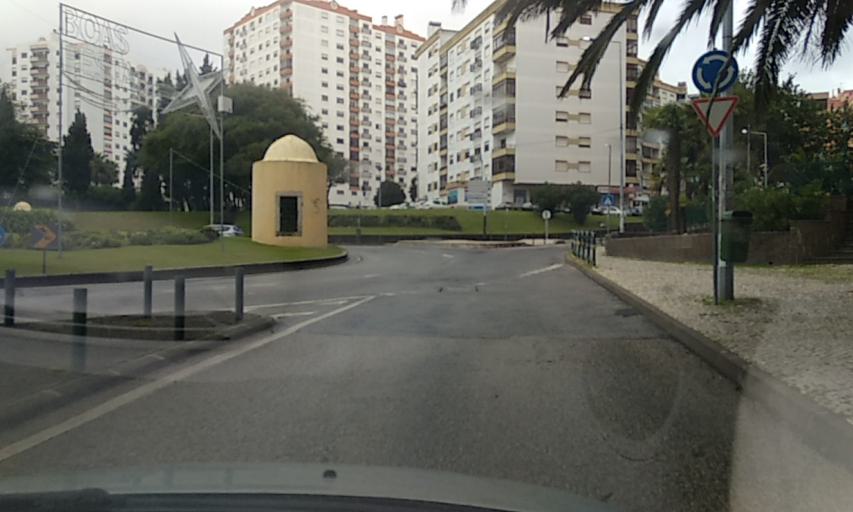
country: PT
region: Lisbon
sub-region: Sintra
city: Cacem
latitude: 38.7544
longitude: -9.2805
